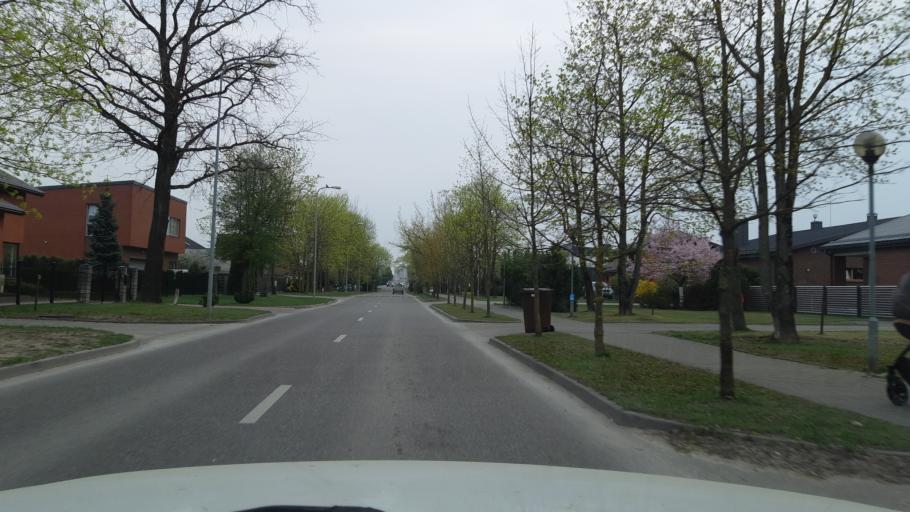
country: LT
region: Kauno apskritis
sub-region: Kaunas
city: Sargenai
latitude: 54.9437
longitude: 23.9033
